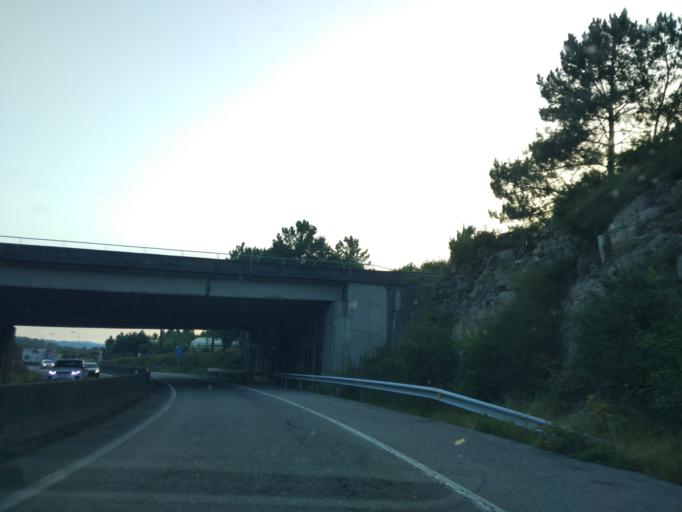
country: ES
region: Galicia
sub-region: Provincia da Coruna
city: Padron
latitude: 42.7346
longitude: -8.6374
